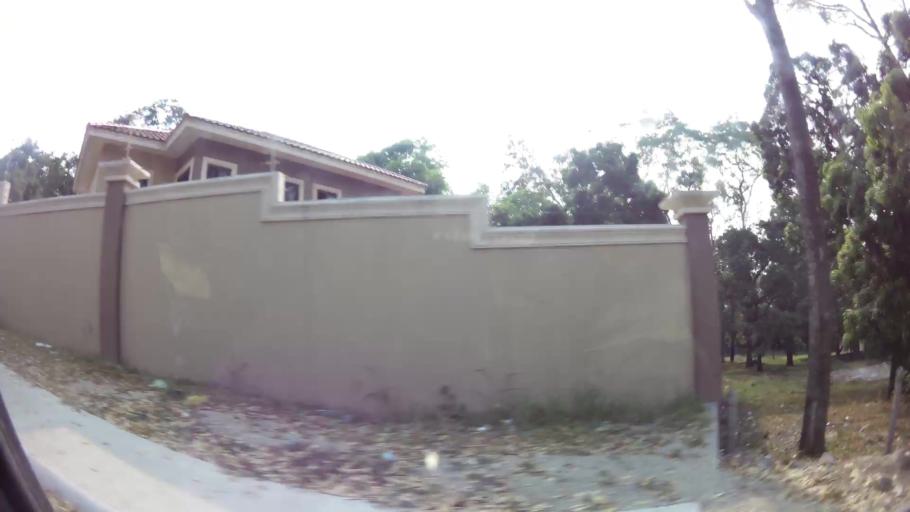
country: HN
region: Cortes
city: El Zapotal del Norte
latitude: 15.5196
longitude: -88.0505
